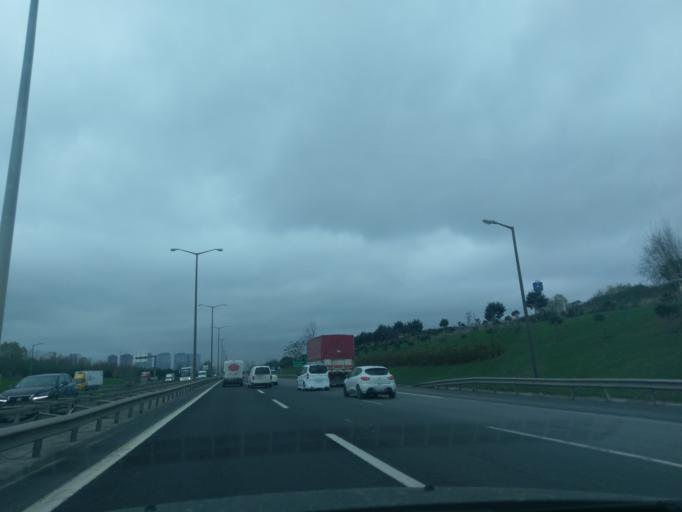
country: TR
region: Istanbul
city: Esenyurt
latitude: 41.0859
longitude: 28.6367
